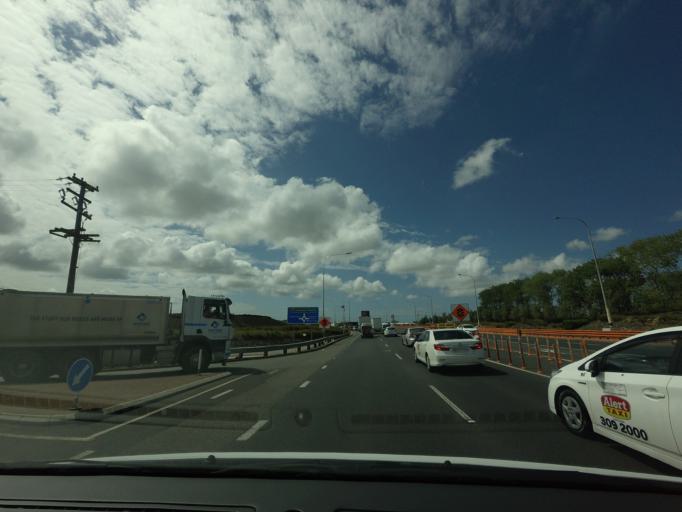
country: NZ
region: Auckland
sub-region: Auckland
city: Mangere
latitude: -36.9940
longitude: 174.7860
